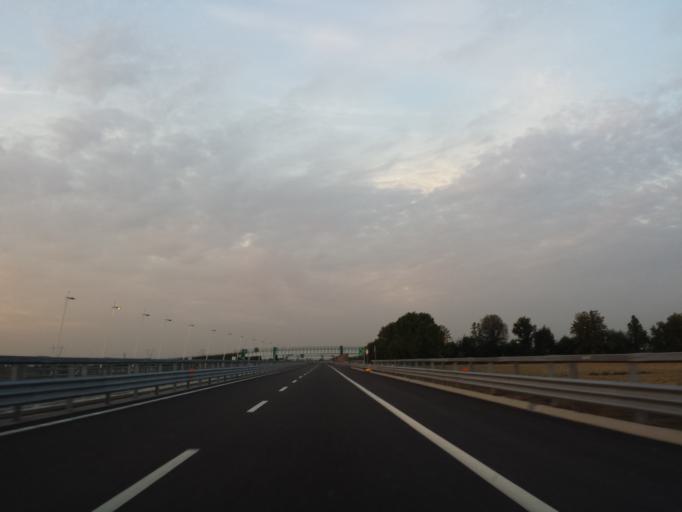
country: IT
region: Veneto
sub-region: Provincia di Vicenza
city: Villaganzerla
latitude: 45.4158
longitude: 11.6346
